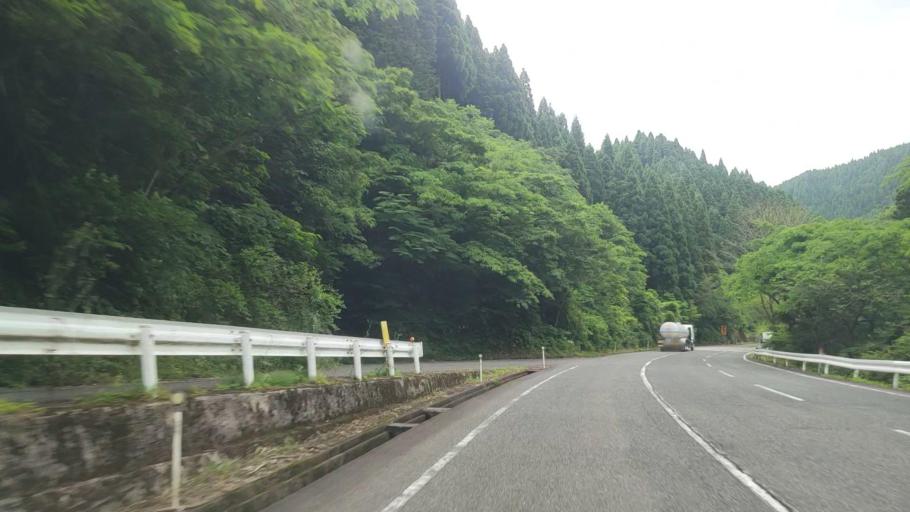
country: JP
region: Tottori
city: Yonago
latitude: 35.2599
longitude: 133.4376
